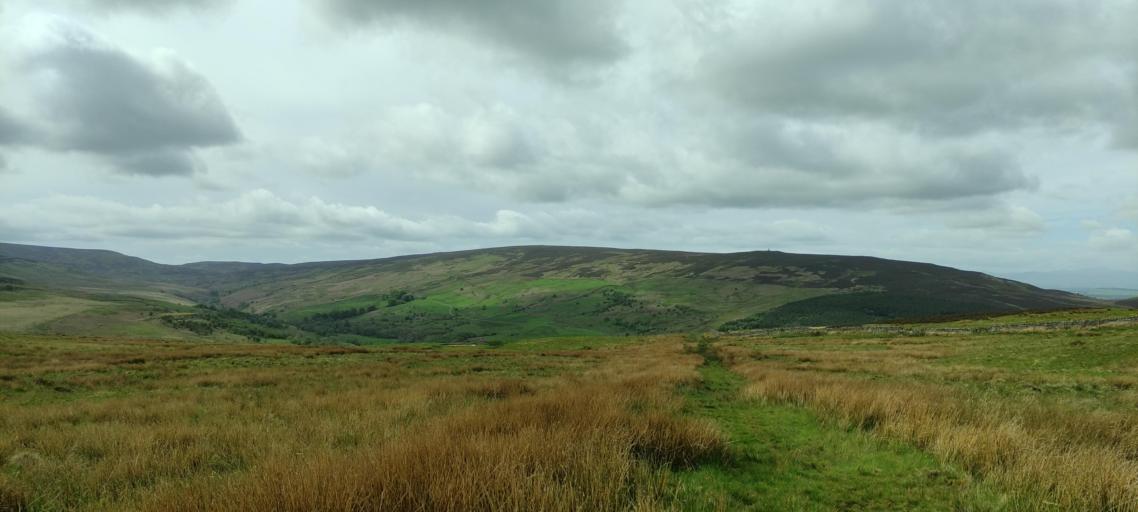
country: GB
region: England
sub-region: Cumbria
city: Brampton
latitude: 54.8978
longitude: -2.6679
